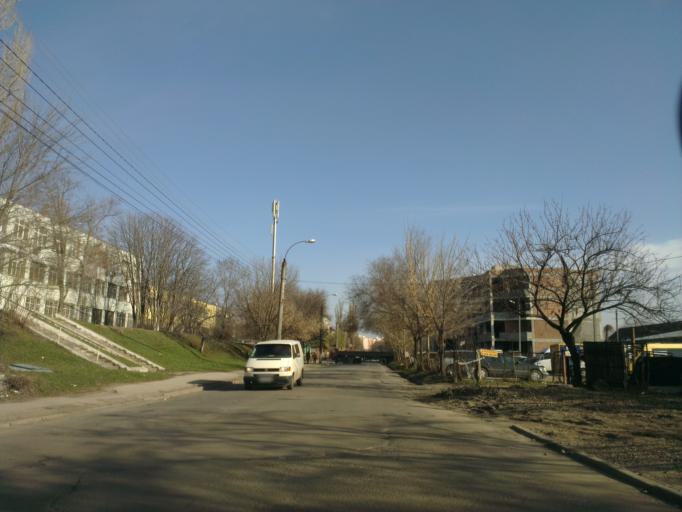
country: MD
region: Chisinau
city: Chisinau
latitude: 47.0201
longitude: 28.8830
